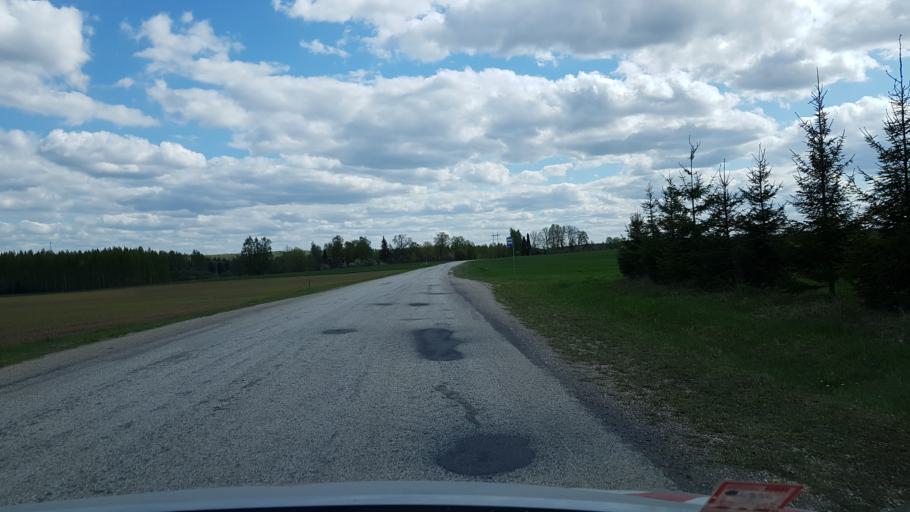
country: EE
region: Tartu
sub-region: UElenurme vald
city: Ulenurme
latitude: 58.2826
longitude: 26.9035
